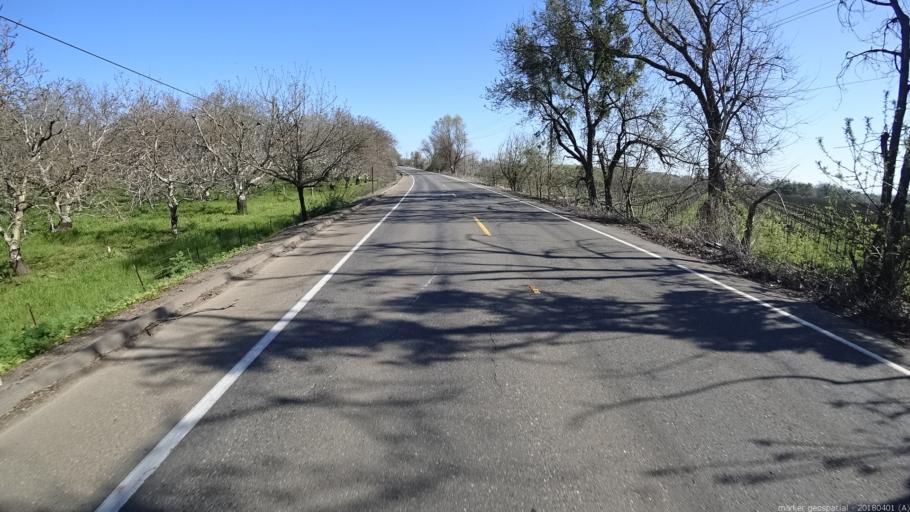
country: US
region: California
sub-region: Sacramento County
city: Rancho Murieta
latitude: 38.4891
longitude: -121.1622
